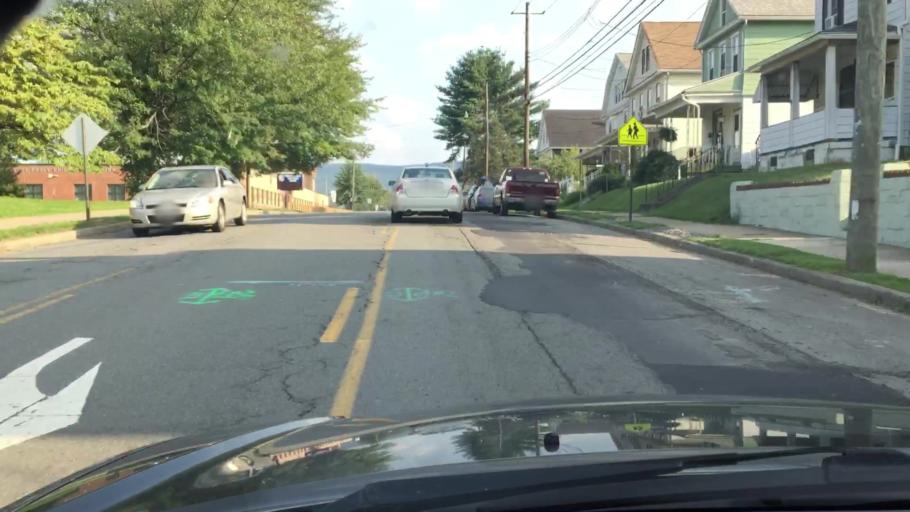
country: US
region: Pennsylvania
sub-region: Luzerne County
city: Nanticoke
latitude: 41.2039
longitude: -75.9926
